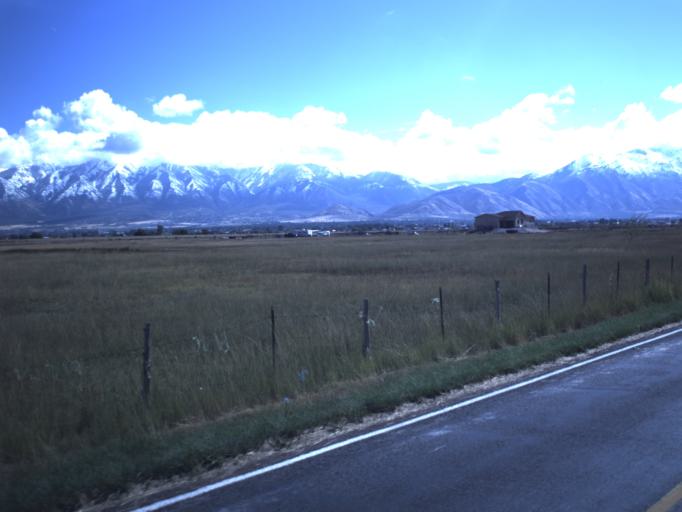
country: US
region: Utah
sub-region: Utah County
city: West Mountain
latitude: 40.0967
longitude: -111.7882
